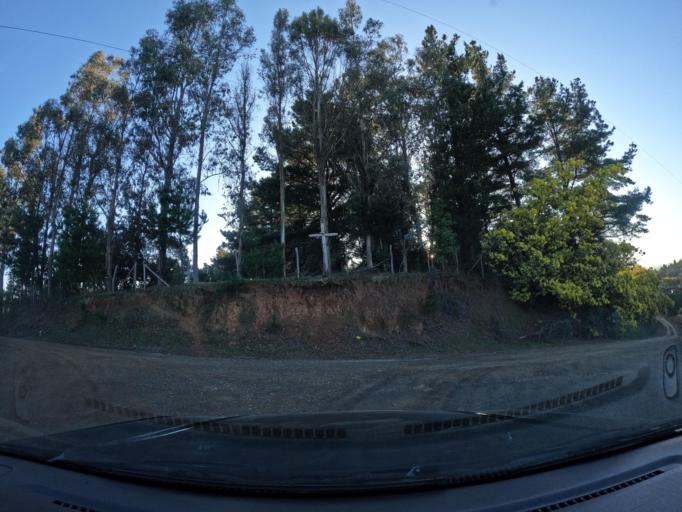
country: CL
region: Biobio
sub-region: Provincia de Concepcion
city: Chiguayante
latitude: -37.0177
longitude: -72.8579
